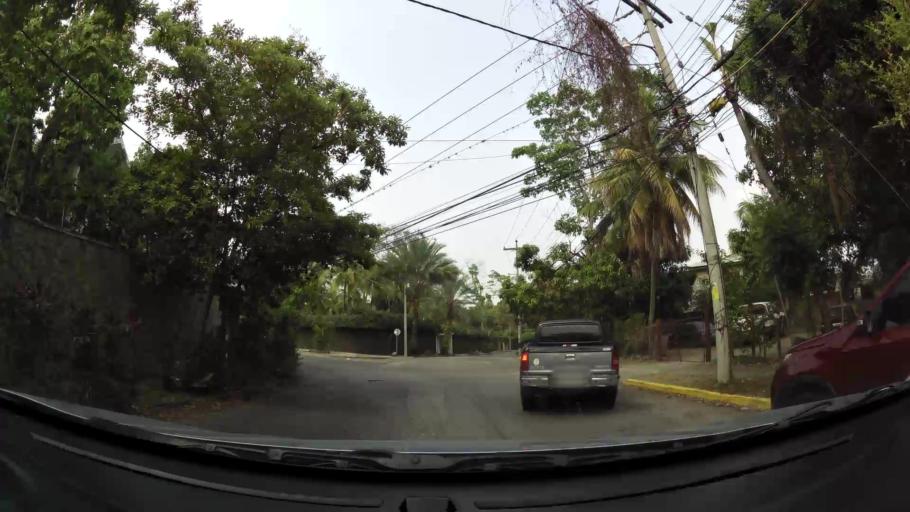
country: HN
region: Cortes
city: Armenta
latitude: 15.5037
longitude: -88.0445
